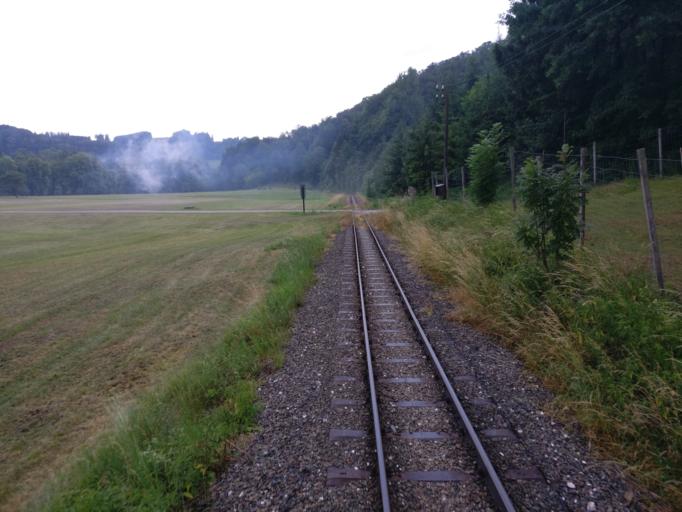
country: AT
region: Upper Austria
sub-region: Politischer Bezirk Kirchdorf an der Krems
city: Gruenburg
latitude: 47.9890
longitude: 14.2802
